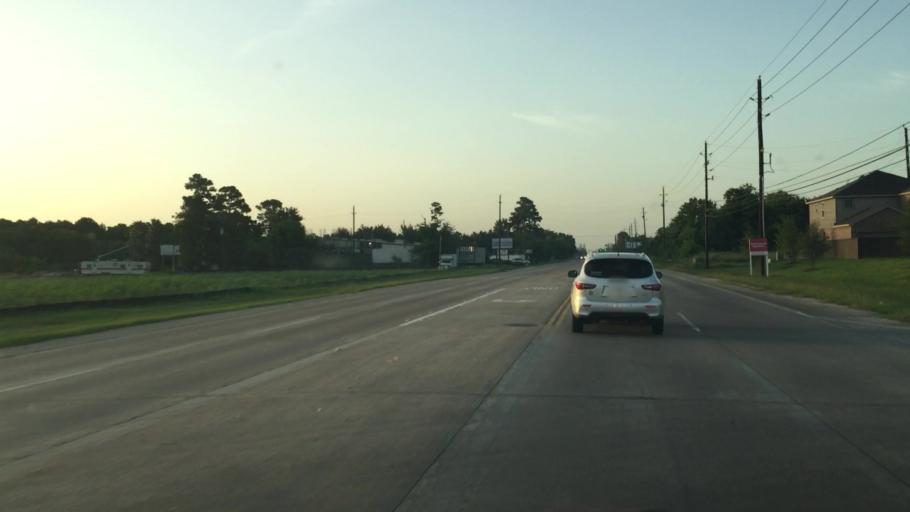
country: US
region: Texas
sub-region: Harris County
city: Hudson
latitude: 29.9973
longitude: -95.5053
